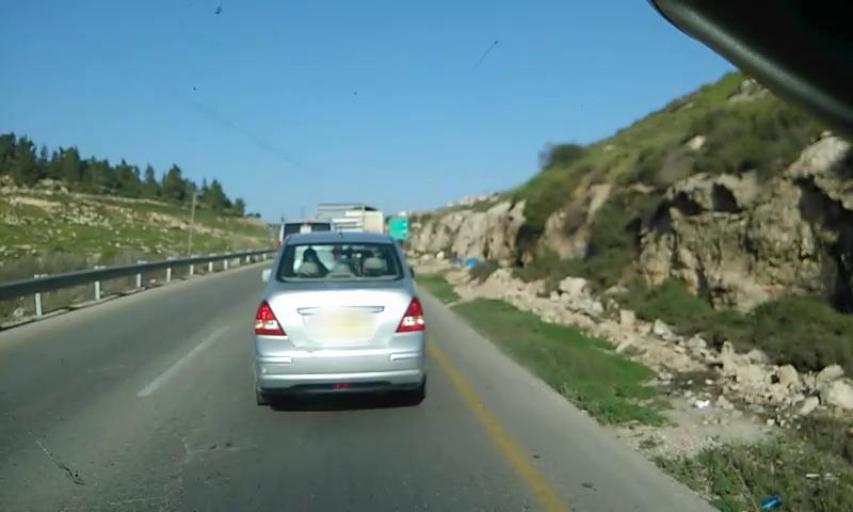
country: PS
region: West Bank
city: Qalqas
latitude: 31.4933
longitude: 35.0738
